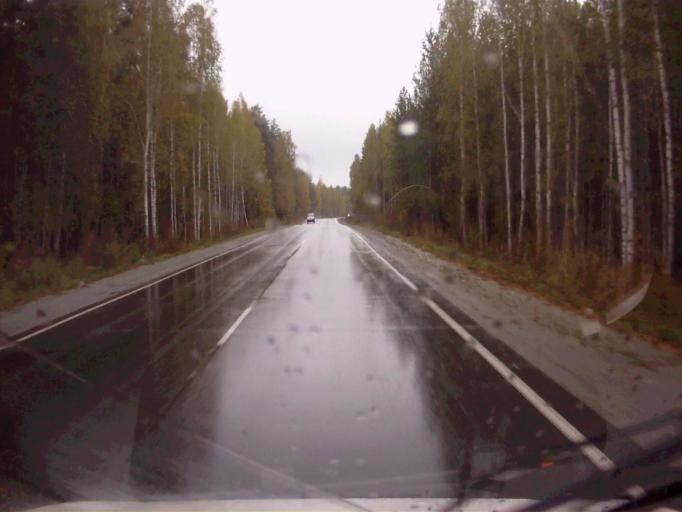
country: RU
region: Chelyabinsk
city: Kyshtym
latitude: 55.6516
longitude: 60.5785
